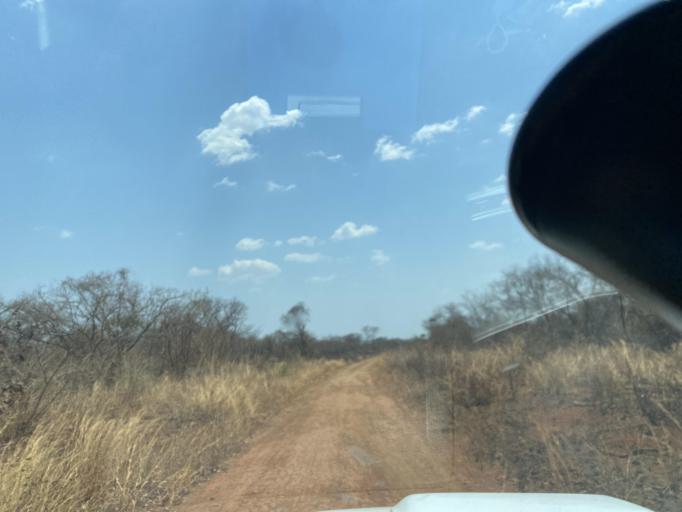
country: ZM
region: Lusaka
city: Lusaka
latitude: -15.5090
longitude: 27.9938
